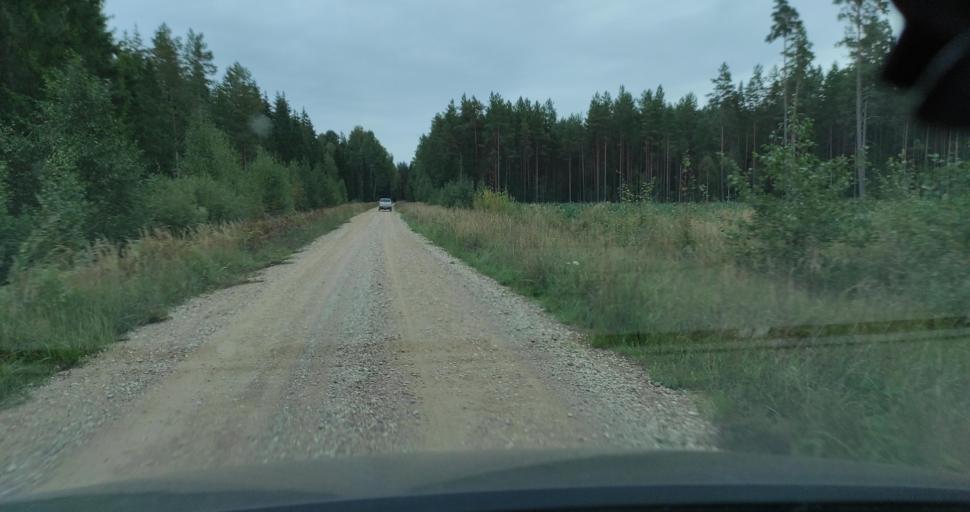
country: LV
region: Talsu Rajons
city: Stende
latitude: 57.0239
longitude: 22.3532
